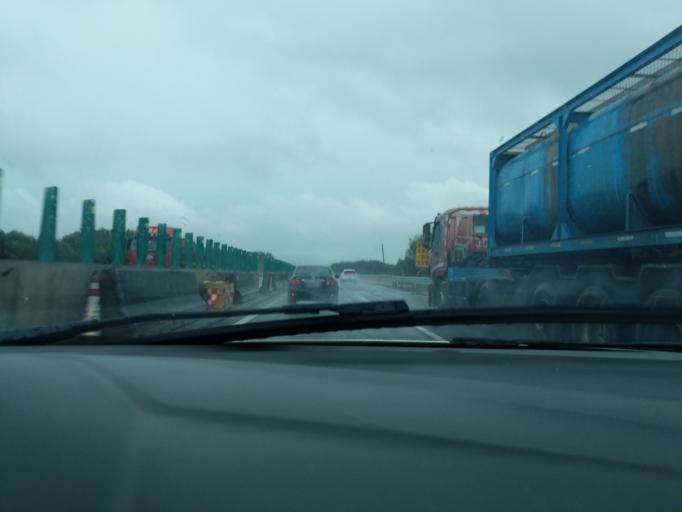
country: CN
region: Guangdong
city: Yueshan
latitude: 22.4630
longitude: 112.7325
